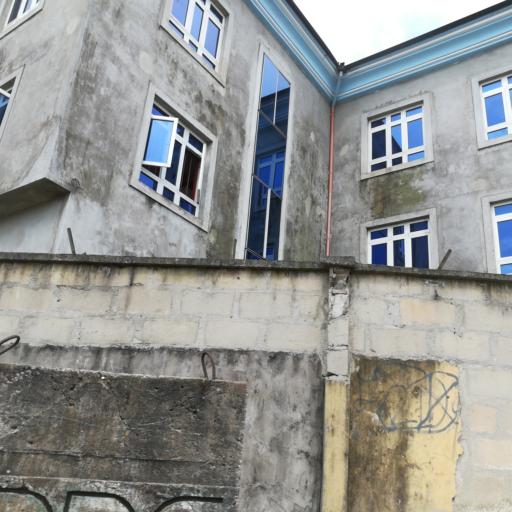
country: NG
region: Rivers
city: Port Harcourt
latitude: 4.8735
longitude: 7.0129
